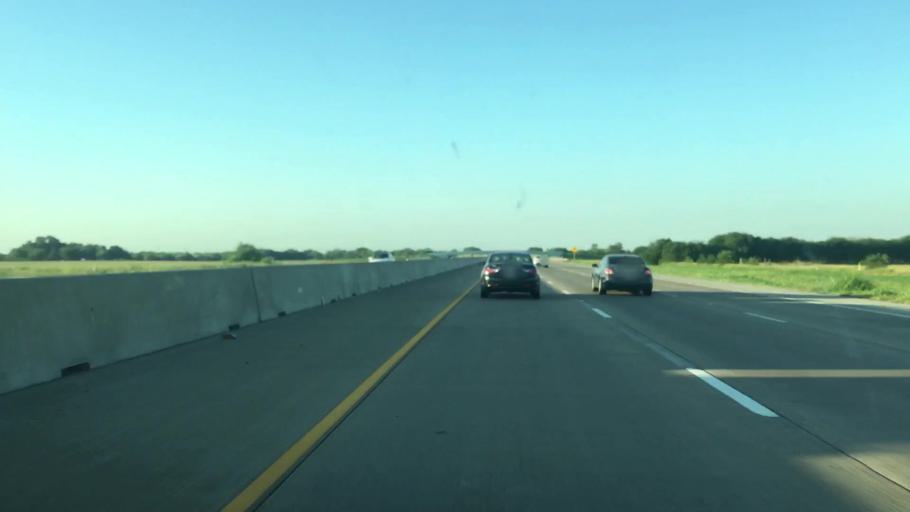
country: US
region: Texas
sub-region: Ellis County
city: Nash
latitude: 32.2912
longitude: -96.8675
